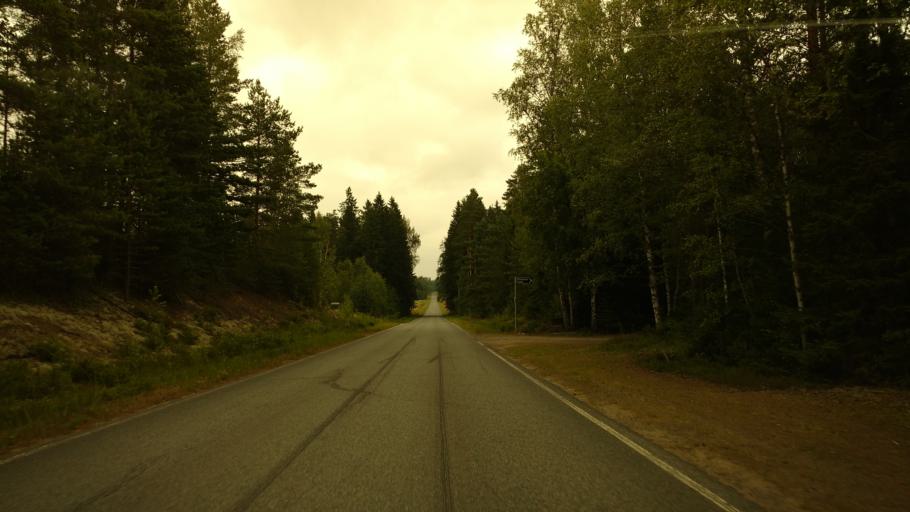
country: FI
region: Haeme
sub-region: Forssa
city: Ypaejae
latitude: 60.7514
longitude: 23.2057
